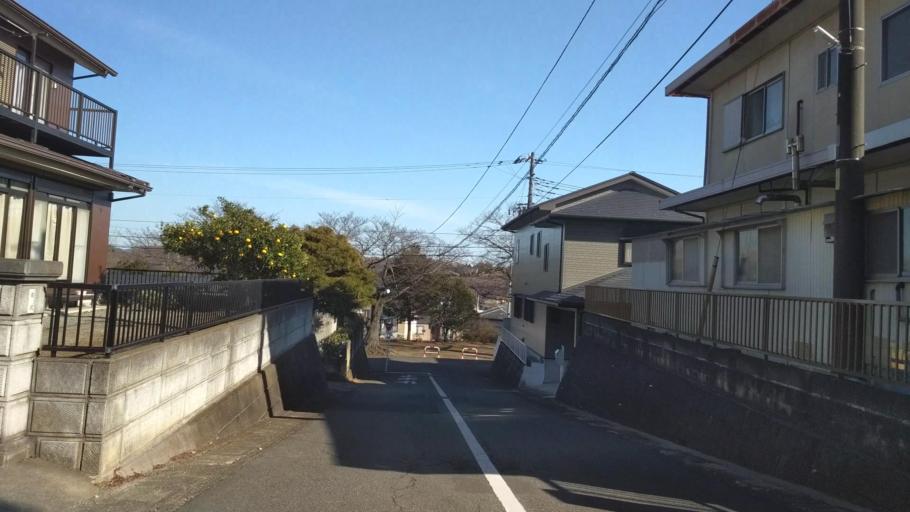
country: JP
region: Kanagawa
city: Hadano
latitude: 35.3461
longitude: 139.2302
